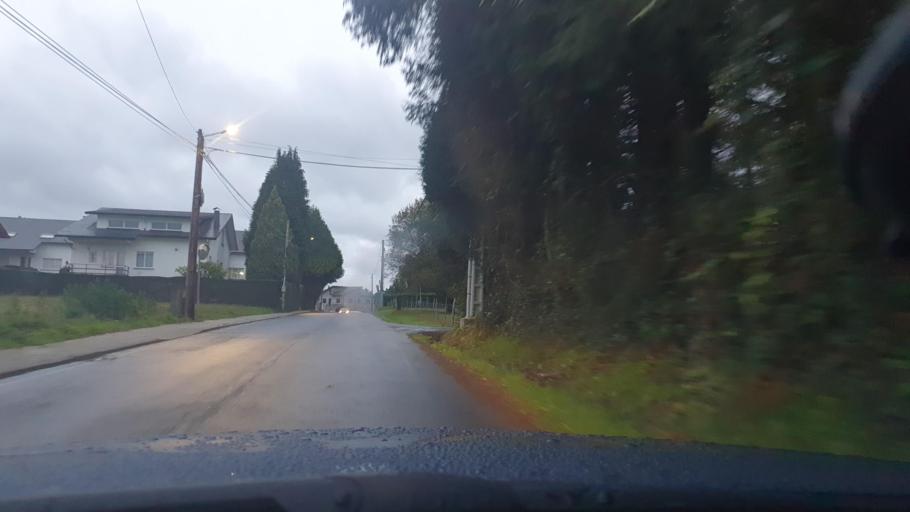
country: ES
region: Galicia
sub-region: Provincia da Coruna
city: Santiago de Compostela
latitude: 42.8487
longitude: -8.5886
